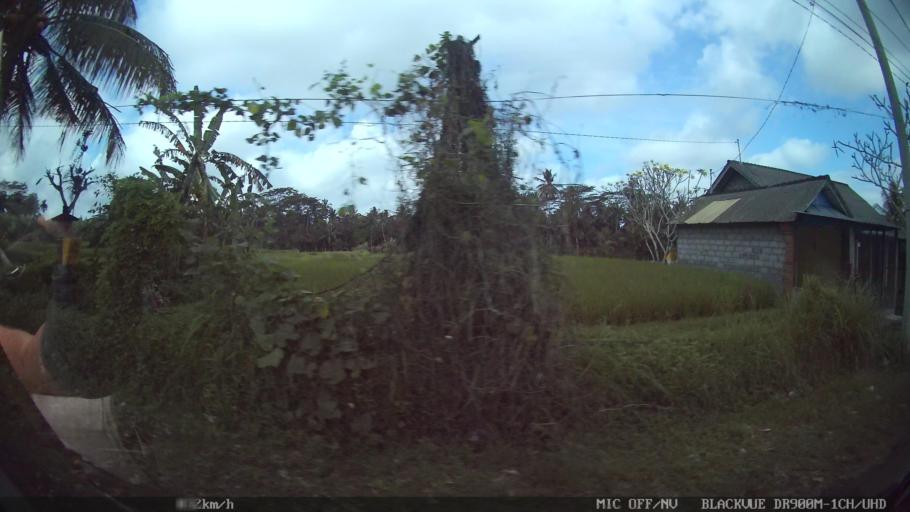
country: ID
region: Bali
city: Banjar Pesalakan
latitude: -8.5018
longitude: 115.3041
